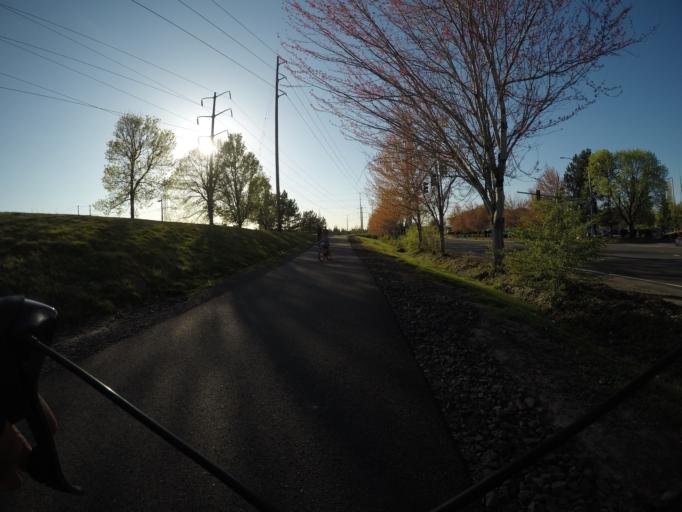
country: US
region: Oregon
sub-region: Washington County
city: Aloha
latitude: 45.5085
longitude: -122.8437
